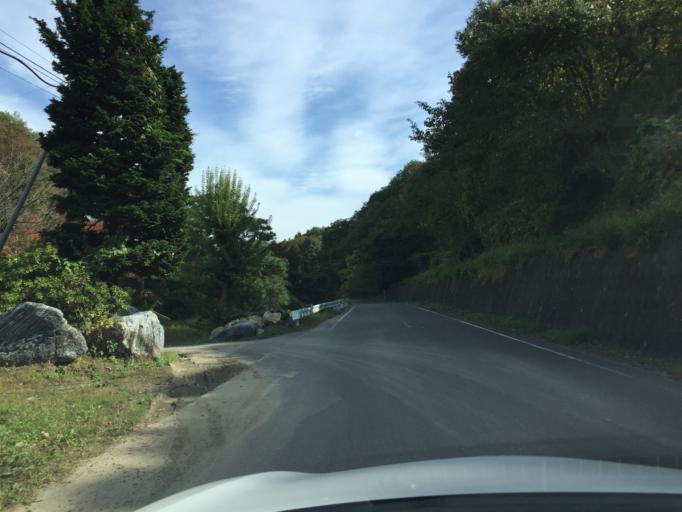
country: JP
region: Fukushima
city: Nihommatsu
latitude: 37.5792
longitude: 140.4890
